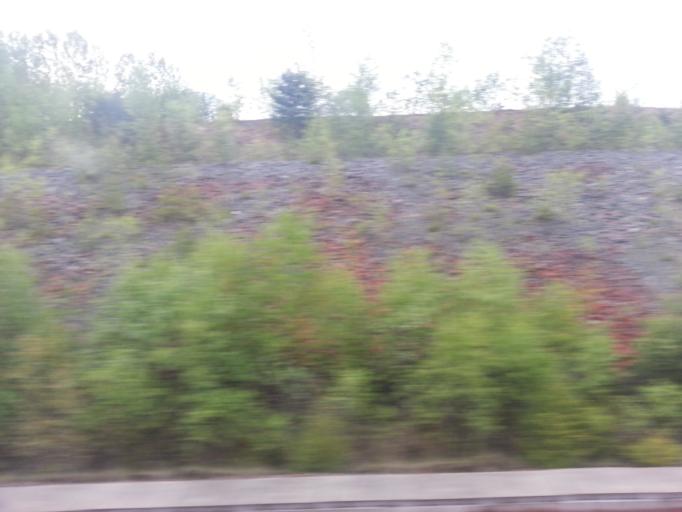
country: NO
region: Akershus
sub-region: Eidsvoll
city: Raholt
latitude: 60.2850
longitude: 11.1659
